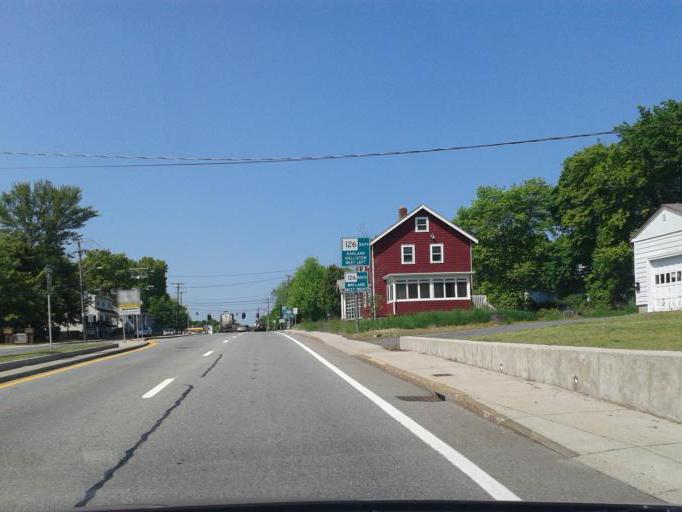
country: US
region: Massachusetts
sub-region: Middlesex County
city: Framingham
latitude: 42.3022
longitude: -71.4044
